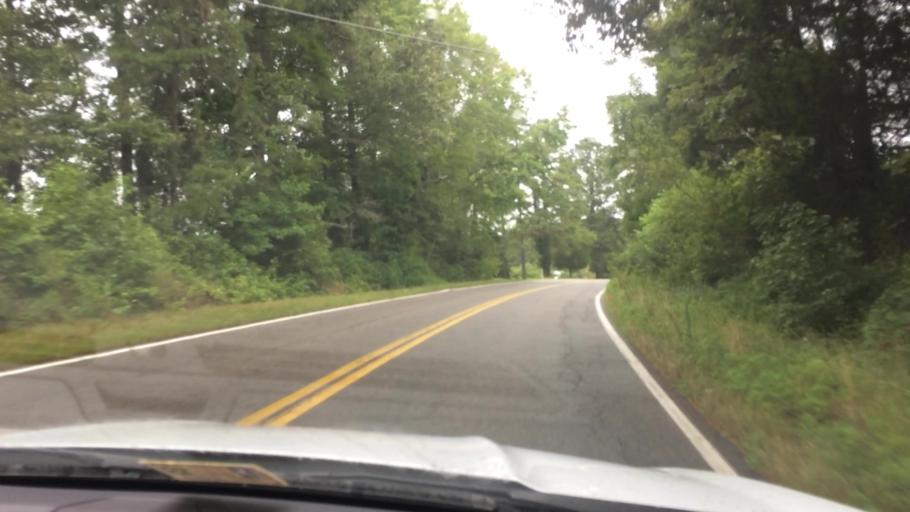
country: US
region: Virginia
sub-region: King William County
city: West Point
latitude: 37.5361
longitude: -76.7493
